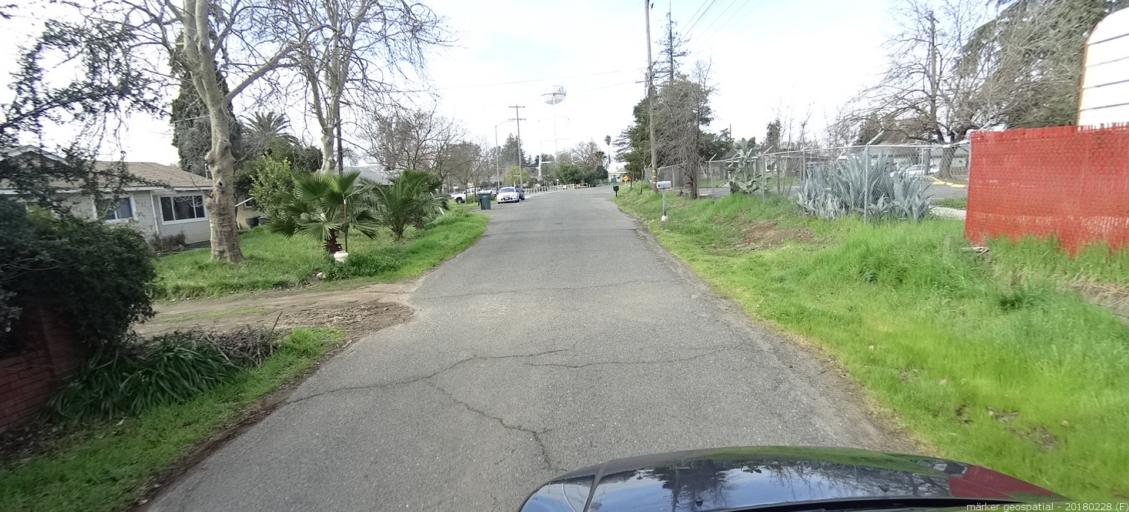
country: US
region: California
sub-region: Sacramento County
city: Rio Linda
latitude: 38.6901
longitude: -121.4470
